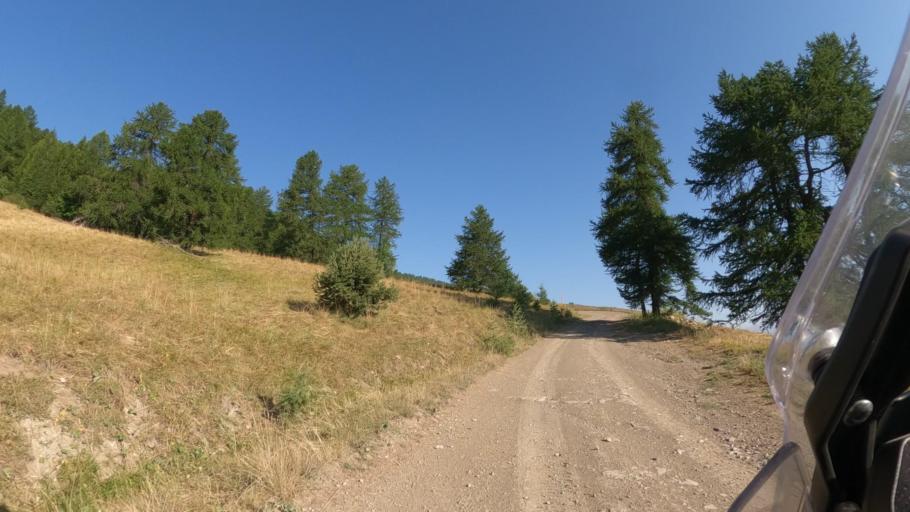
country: FR
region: Provence-Alpes-Cote d'Azur
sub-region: Departement des Hautes-Alpes
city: Guillestre
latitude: 44.6190
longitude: 6.6277
